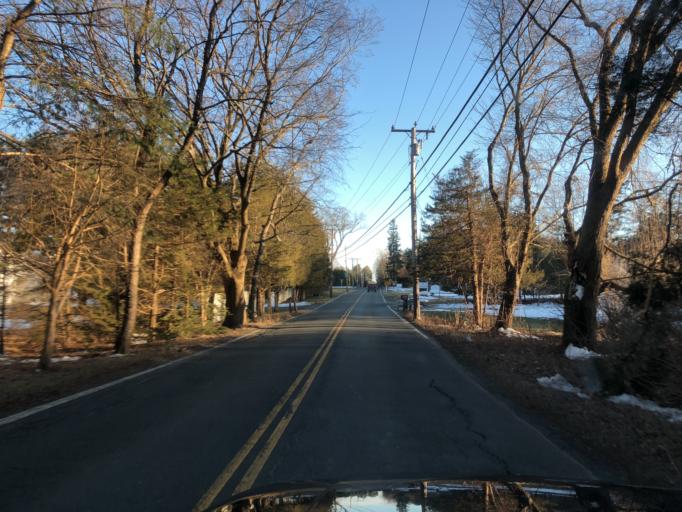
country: US
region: Connecticut
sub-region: Hartford County
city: Farmington
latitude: 41.7676
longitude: -72.8592
